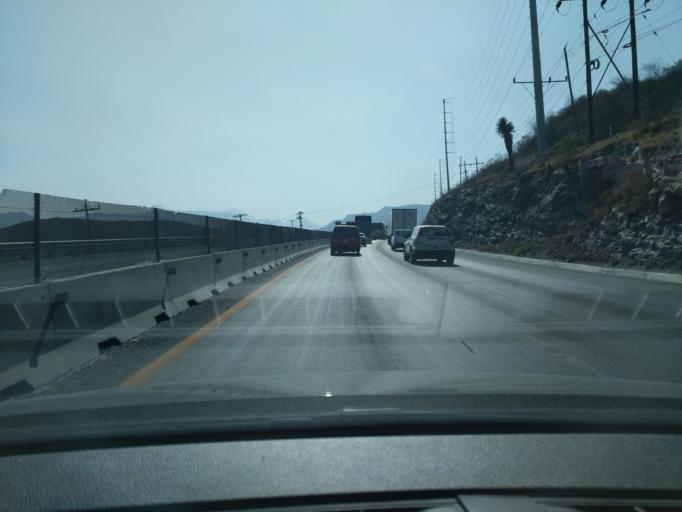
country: MX
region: Nuevo Leon
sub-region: Garcia
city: Los Parques
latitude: 25.7543
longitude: -100.5011
